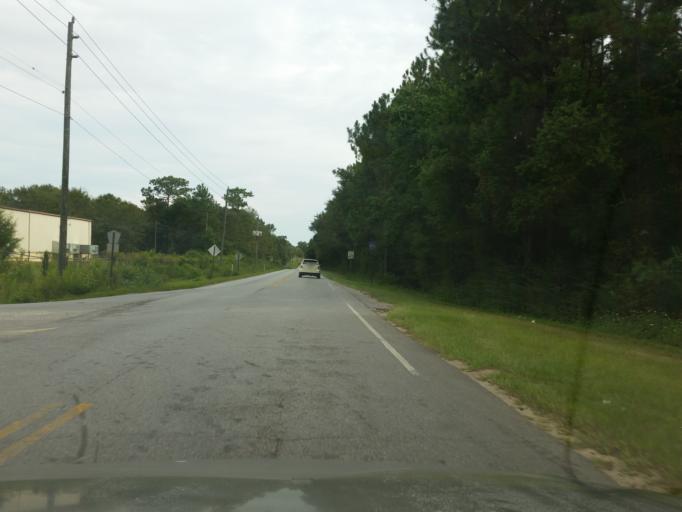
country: US
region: Florida
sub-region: Escambia County
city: Cantonment
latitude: 30.6505
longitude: -87.3212
